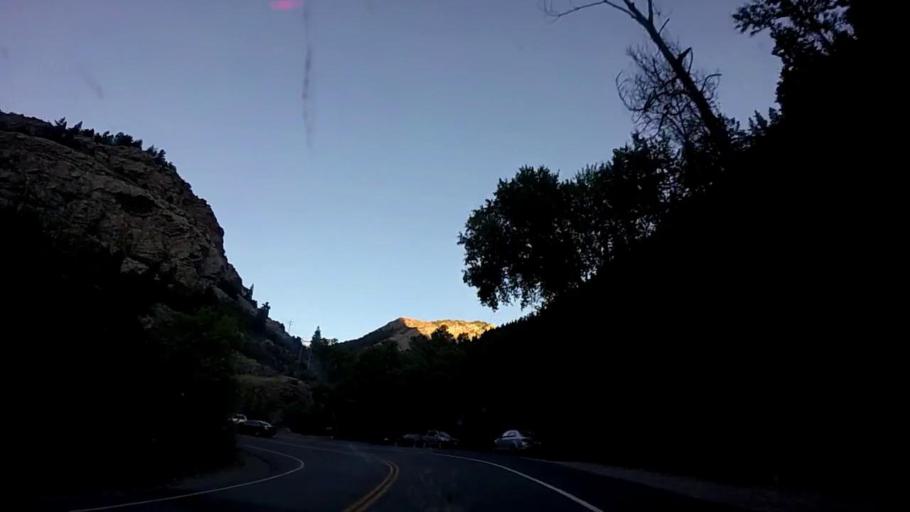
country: US
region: Utah
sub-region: Salt Lake County
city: Mount Olympus
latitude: 40.6337
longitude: -111.7245
